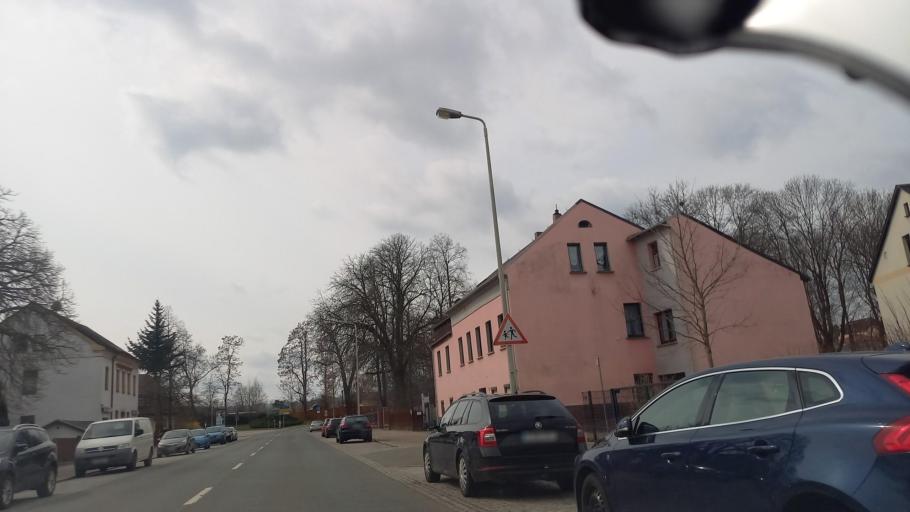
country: DE
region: Saxony
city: Zwickau
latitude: 50.7016
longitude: 12.4980
